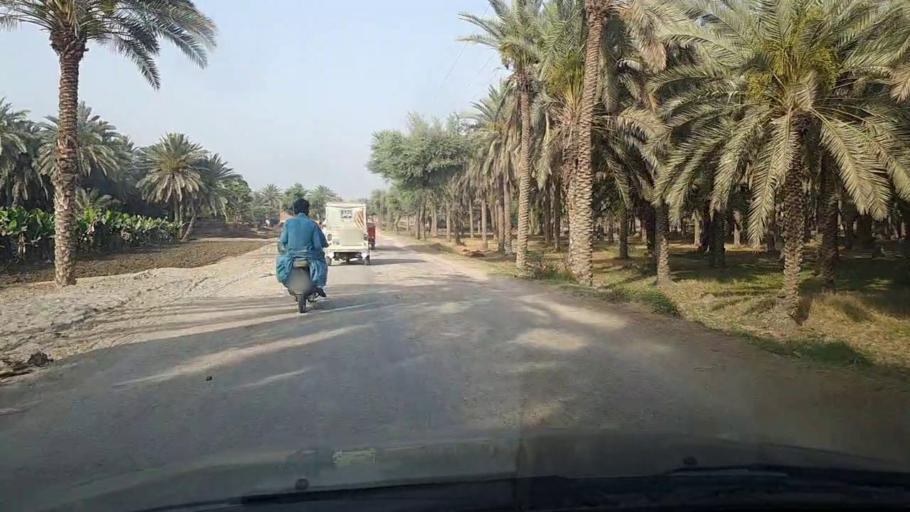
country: PK
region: Sindh
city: Pir jo Goth
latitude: 27.5602
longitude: 68.5659
